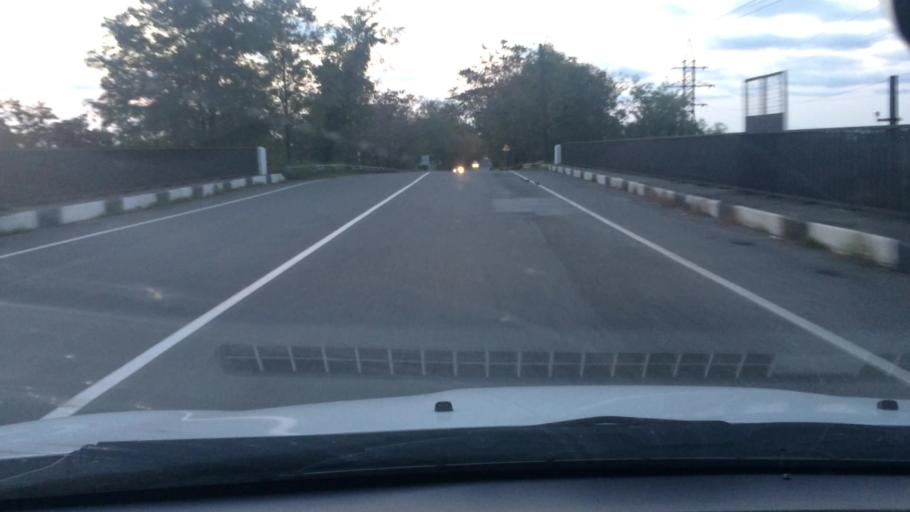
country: GE
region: Guria
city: Urek'i
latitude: 42.0120
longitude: 41.7779
